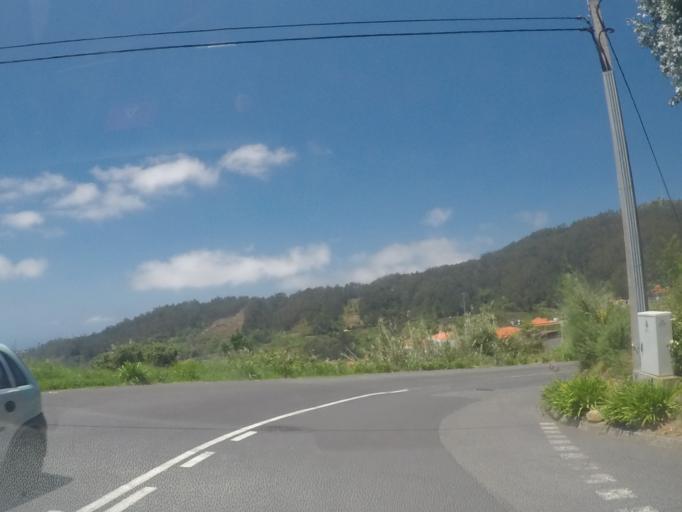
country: PT
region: Madeira
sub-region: Camara de Lobos
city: Curral das Freiras
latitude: 32.6851
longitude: -16.9867
